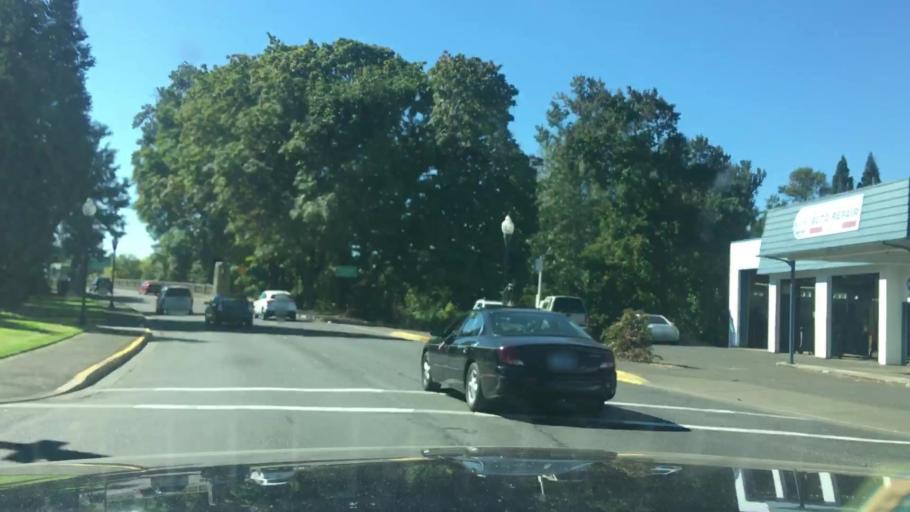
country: US
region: Oregon
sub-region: Lane County
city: Springfield
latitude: 44.0462
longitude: -123.0248
